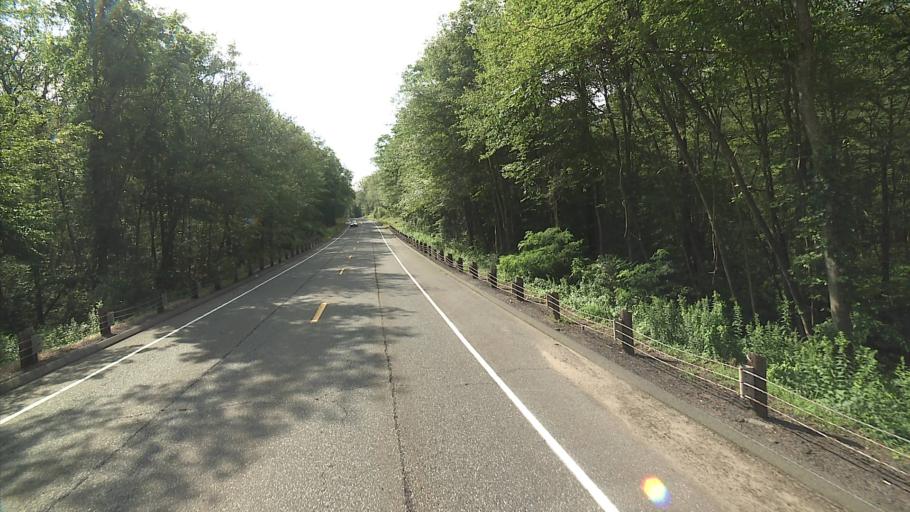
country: US
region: Connecticut
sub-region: Middlesex County
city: Chester Center
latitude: 41.3719
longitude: -72.5007
